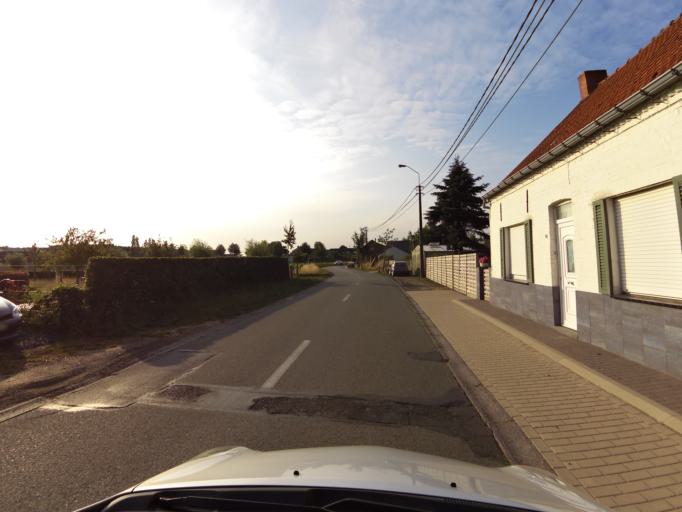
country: BE
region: Flanders
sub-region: Provincie West-Vlaanderen
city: Torhout
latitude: 51.1006
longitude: 3.0837
